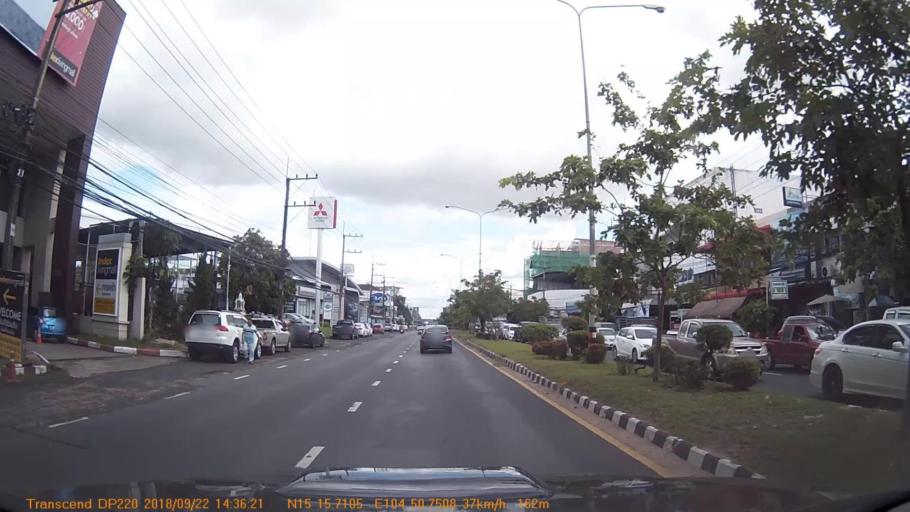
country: TH
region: Changwat Ubon Ratchathani
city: Ubon Ratchathani
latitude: 15.2616
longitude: 104.8460
